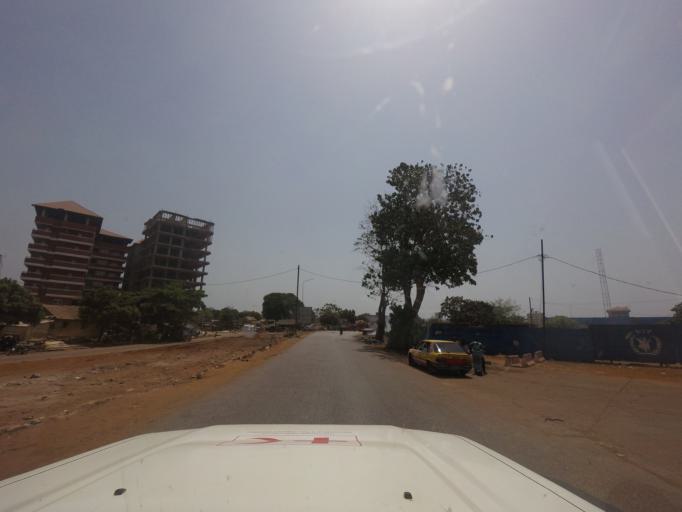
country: GN
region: Conakry
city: Camayenne
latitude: 9.5179
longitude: -13.6982
